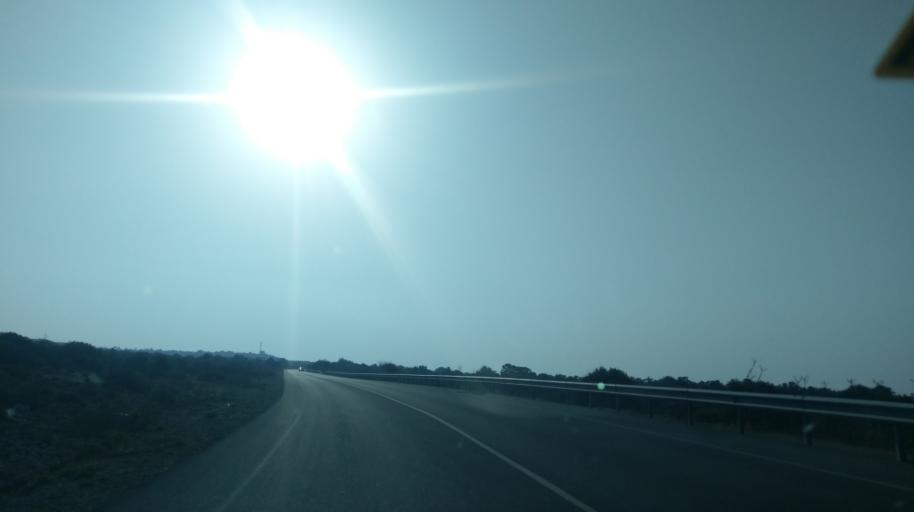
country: CY
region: Ammochostos
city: Leonarisso
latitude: 35.5528
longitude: 34.2109
